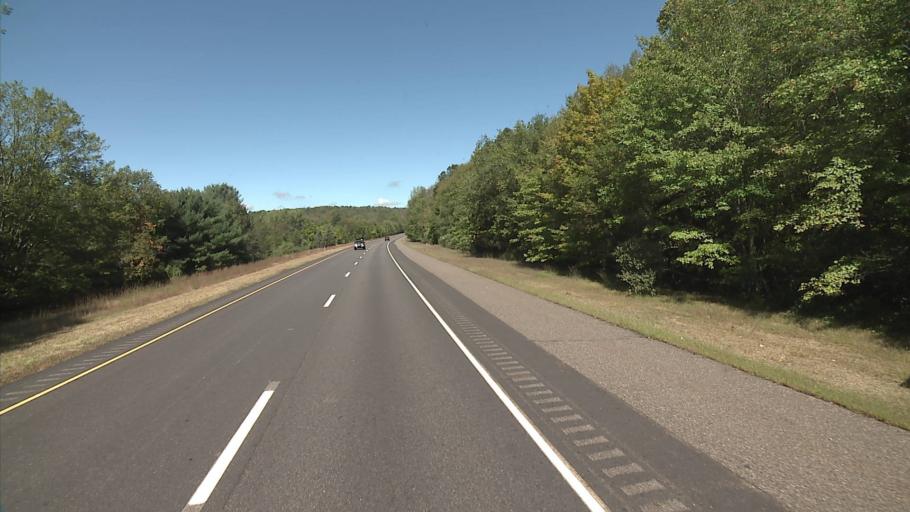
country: US
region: Connecticut
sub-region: New London County
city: Colchester
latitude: 41.4749
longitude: -72.2934
